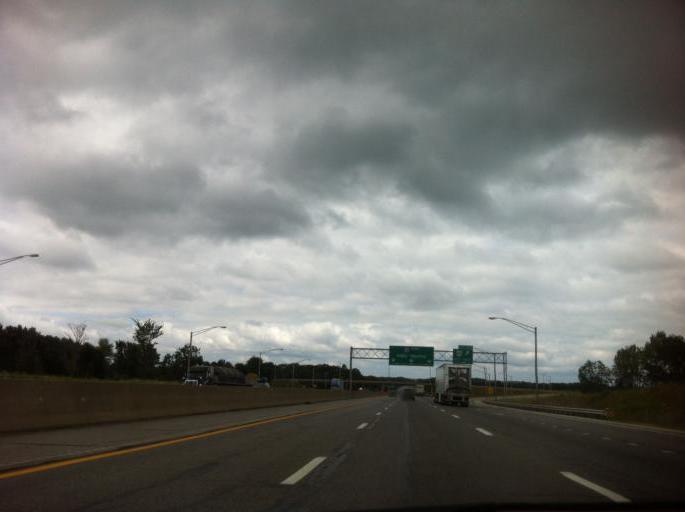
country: US
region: Ohio
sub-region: Portage County
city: Mantua
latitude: 41.2450
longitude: -81.2328
